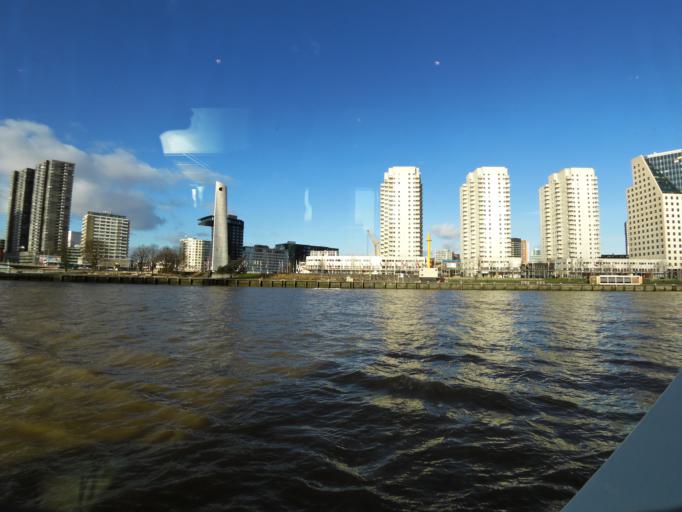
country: NL
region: South Holland
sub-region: Gemeente Rotterdam
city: Rotterdam
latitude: 51.9116
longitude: 4.4868
